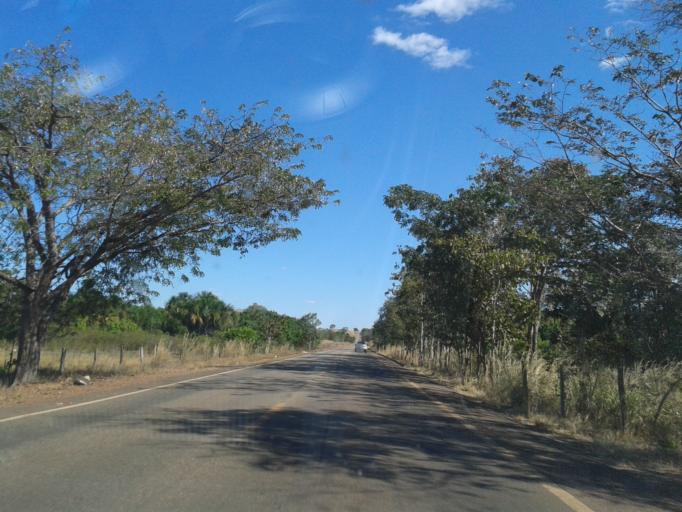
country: BR
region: Goias
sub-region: Crixas
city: Crixas
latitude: -14.1279
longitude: -50.3502
